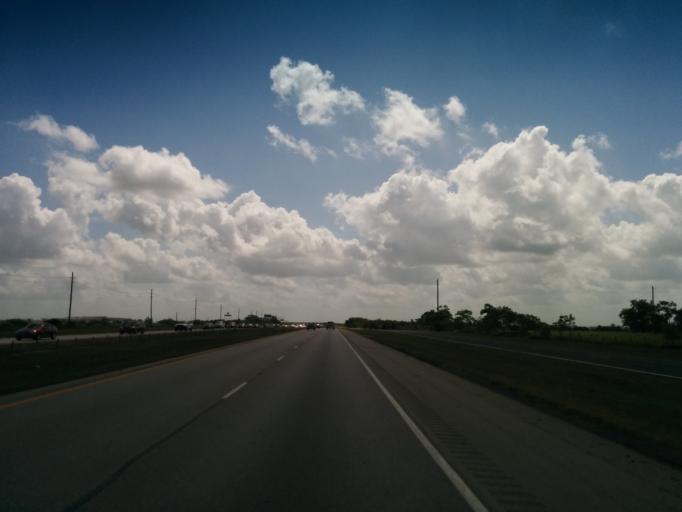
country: US
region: Texas
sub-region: Austin County
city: Sealy
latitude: 29.7566
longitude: -96.2339
